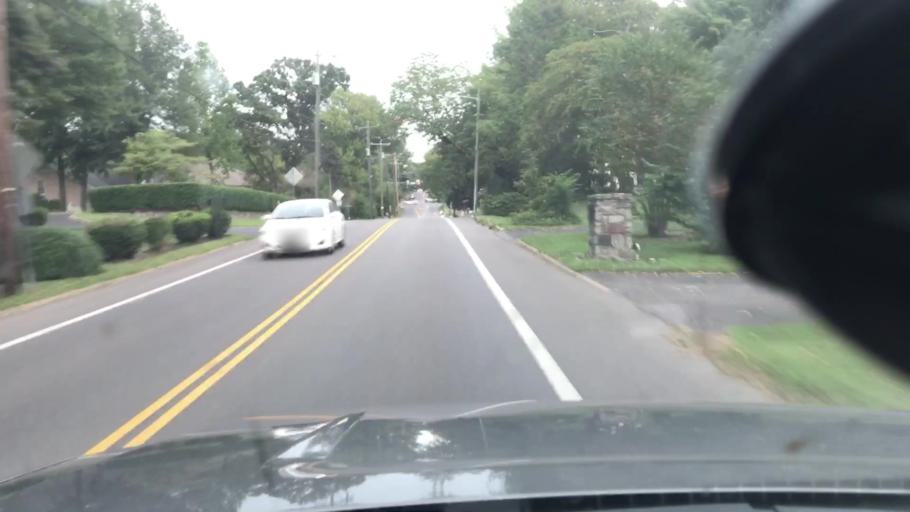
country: US
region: Tennessee
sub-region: Davidson County
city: Belle Meade
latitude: 36.1167
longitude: -86.8392
